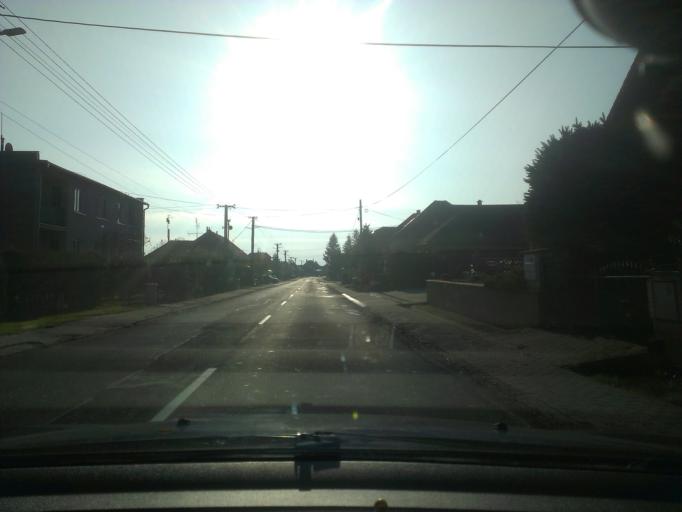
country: SK
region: Trnavsky
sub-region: Okres Trnava
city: Piestany
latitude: 48.5228
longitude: 17.9684
